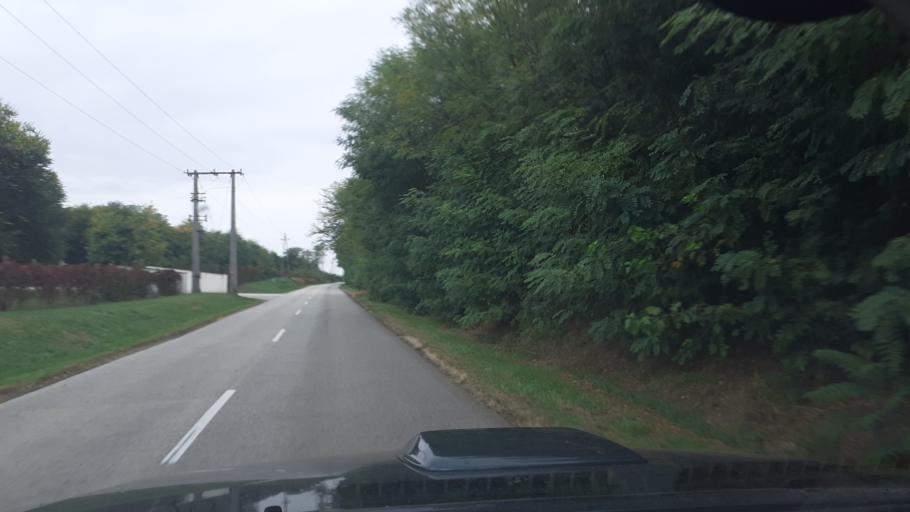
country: HU
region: Tolna
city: Dunafoldvar
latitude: 46.8338
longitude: 18.9011
